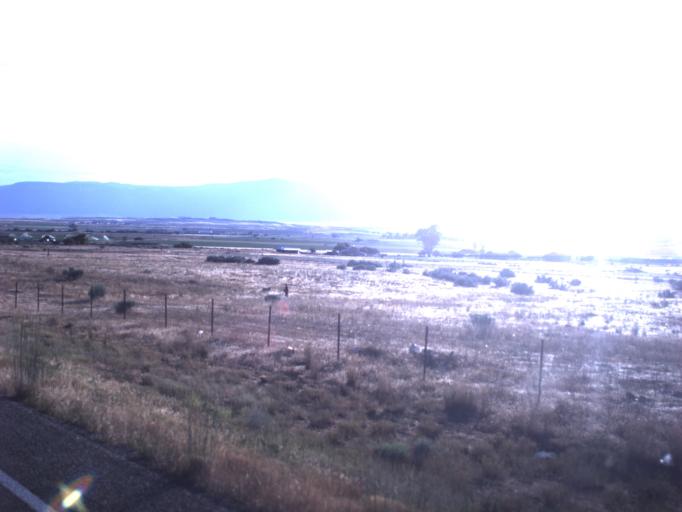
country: US
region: Utah
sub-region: Sanpete County
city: Mount Pleasant
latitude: 39.5227
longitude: -111.4779
